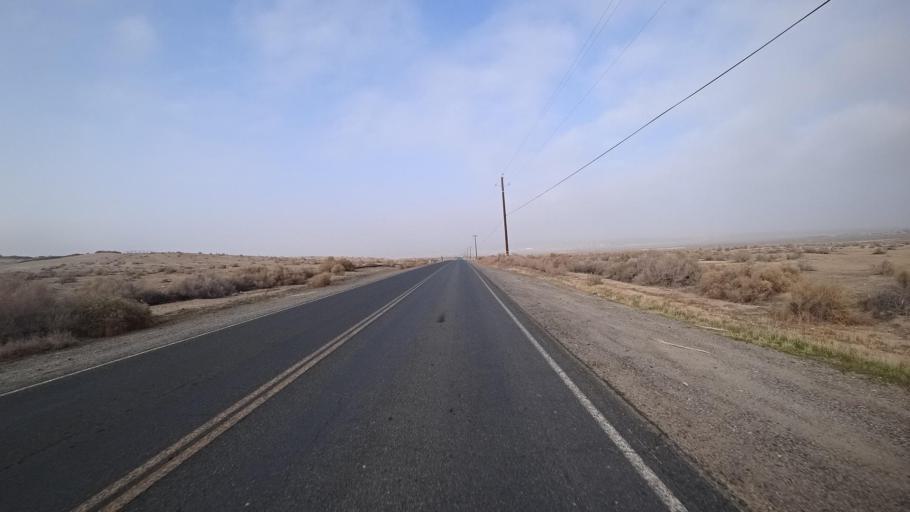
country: US
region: California
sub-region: Kern County
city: Ford City
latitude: 35.2026
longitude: -119.4456
